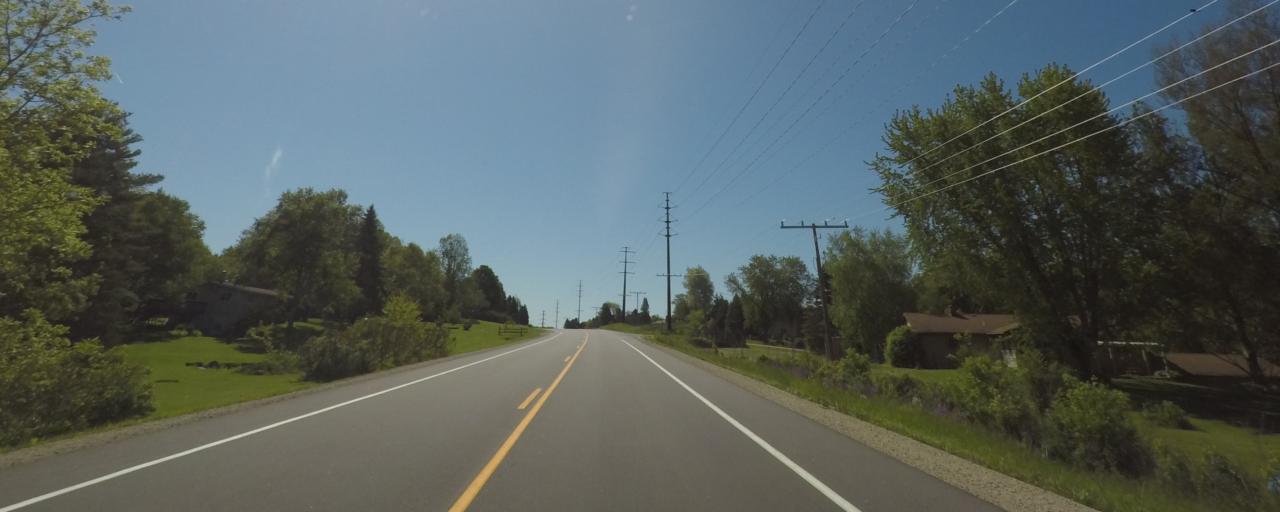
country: US
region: Wisconsin
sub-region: Dane County
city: Fitchburg
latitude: 42.9688
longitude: -89.4963
